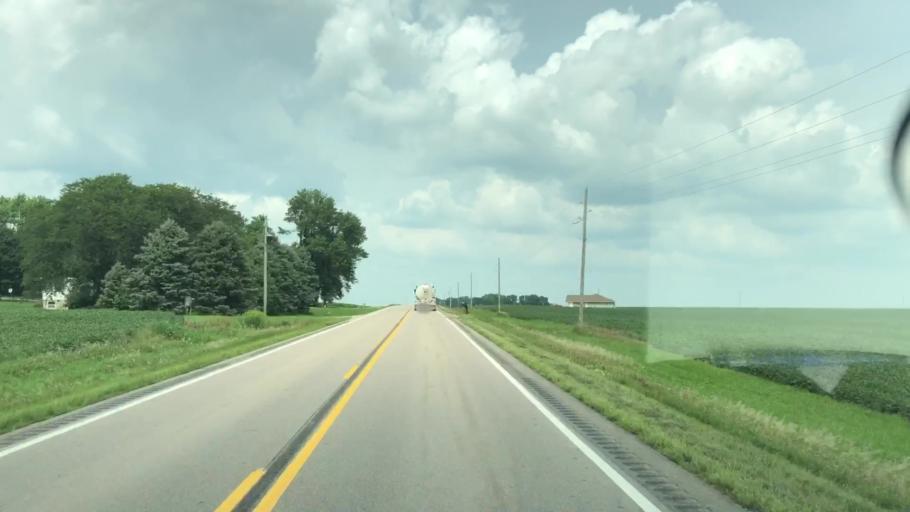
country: US
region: Iowa
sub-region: Plymouth County
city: Remsen
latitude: 42.7899
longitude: -95.9578
